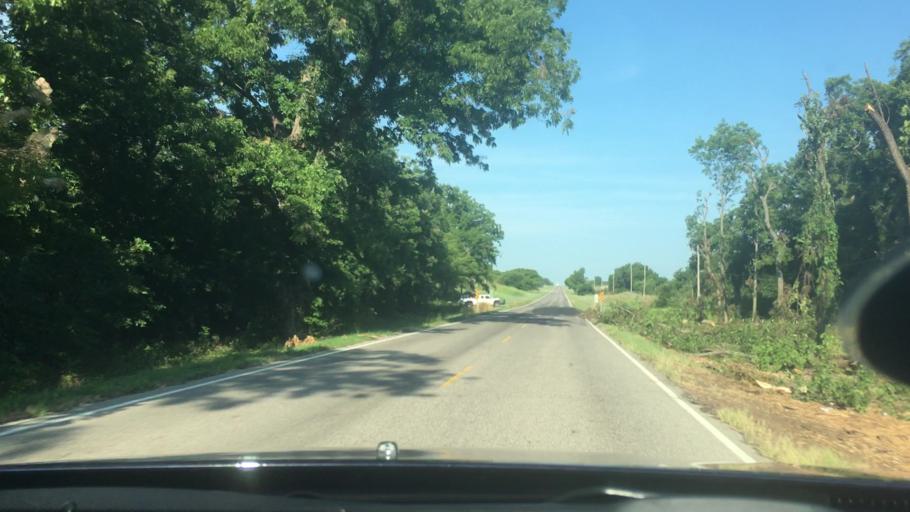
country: US
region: Oklahoma
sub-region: Garvin County
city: Pauls Valley
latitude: 34.6521
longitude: -97.3259
